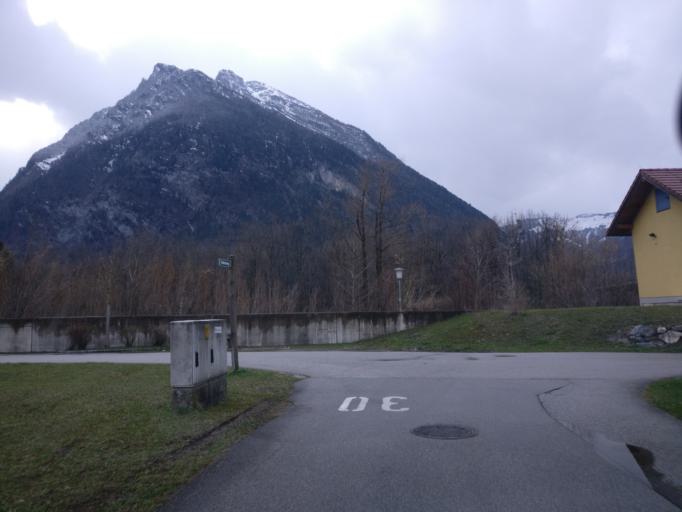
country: AT
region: Salzburg
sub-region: Politischer Bezirk Hallein
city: Golling an der Salzach
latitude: 47.5909
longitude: 13.1643
